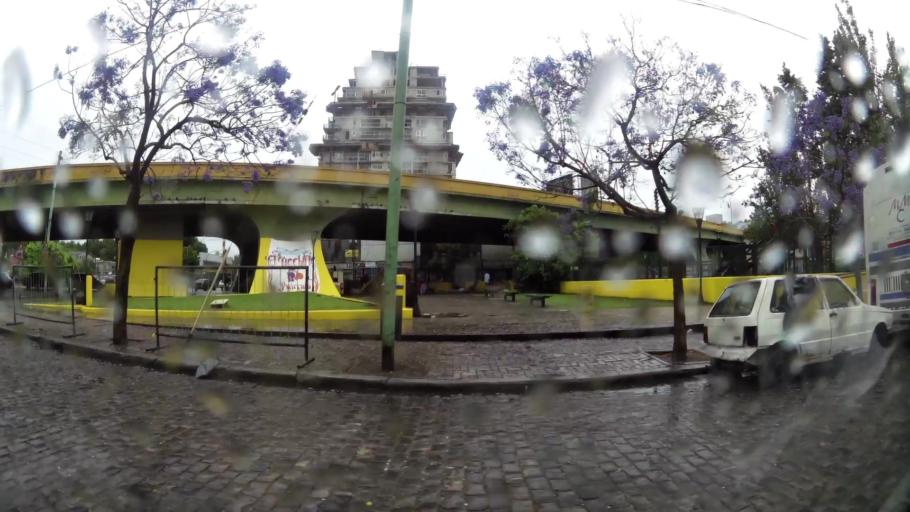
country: AR
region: Buenos Aires F.D.
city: Colegiales
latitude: -34.5888
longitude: -58.4380
